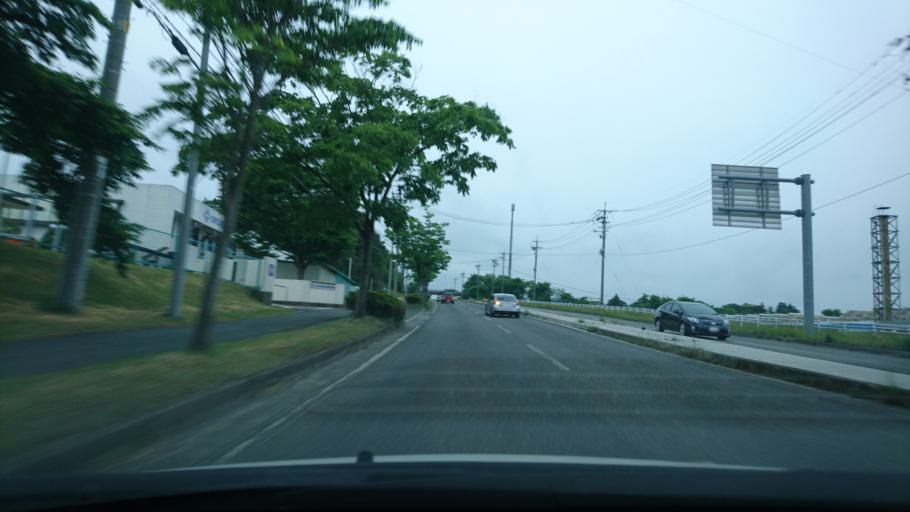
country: JP
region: Iwate
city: Ichinoseki
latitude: 38.9182
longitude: 141.1590
